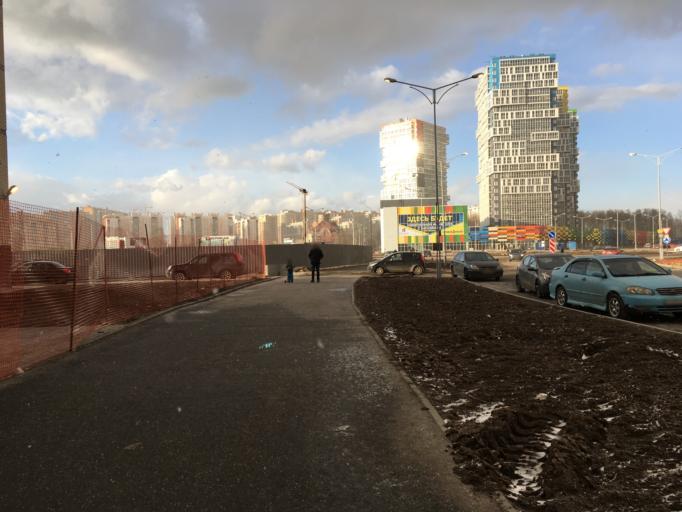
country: RU
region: Leningrad
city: Rybatskoye
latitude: 59.9076
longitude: 30.5127
